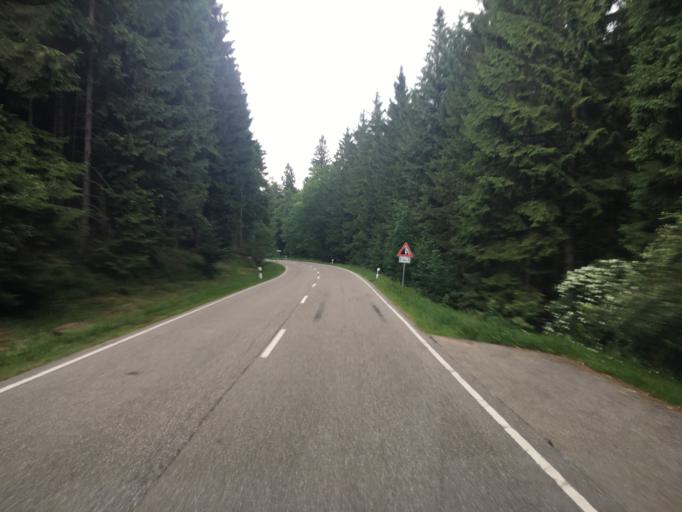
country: DE
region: Baden-Wuerttemberg
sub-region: Karlsruhe Region
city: Buhlertal
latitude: 48.6732
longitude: 8.2342
